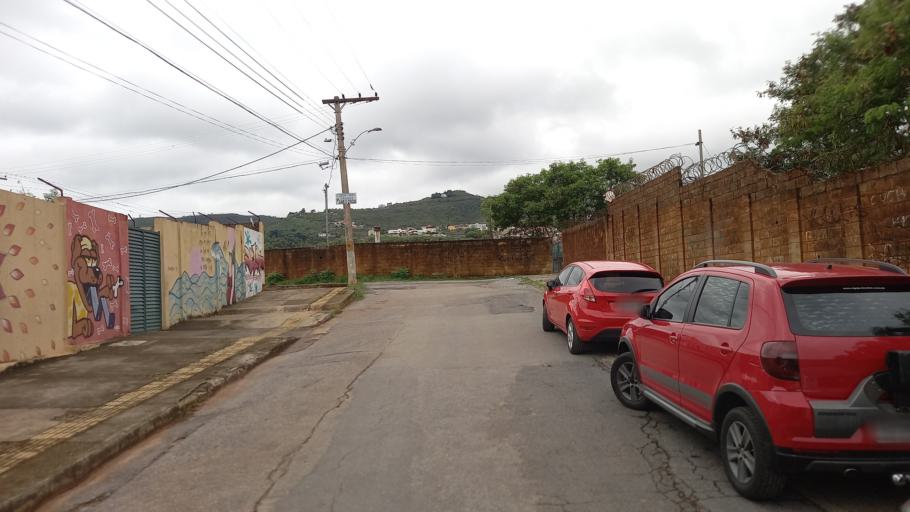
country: BR
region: Minas Gerais
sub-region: Belo Horizonte
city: Belo Horizonte
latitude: -19.9191
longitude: -43.8881
